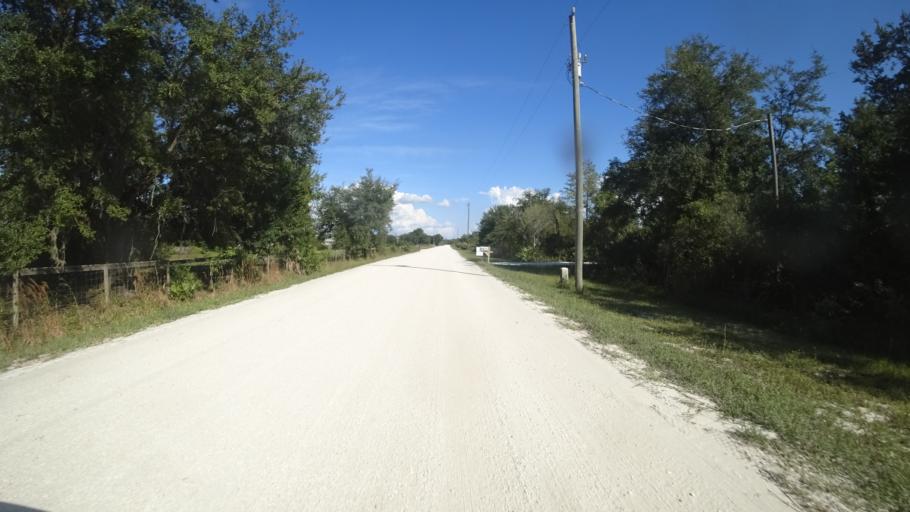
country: US
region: Florida
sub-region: Sarasota County
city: The Meadows
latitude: 27.4267
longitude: -82.2670
